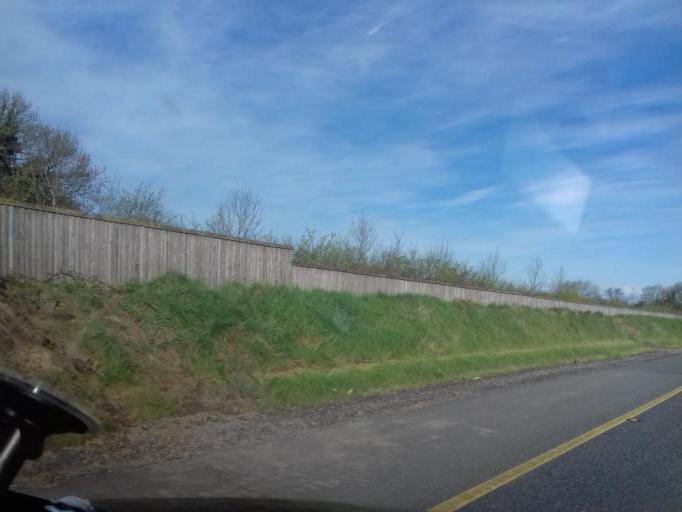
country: IE
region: Leinster
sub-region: An Mhi
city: Navan
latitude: 53.6484
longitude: -6.7499
